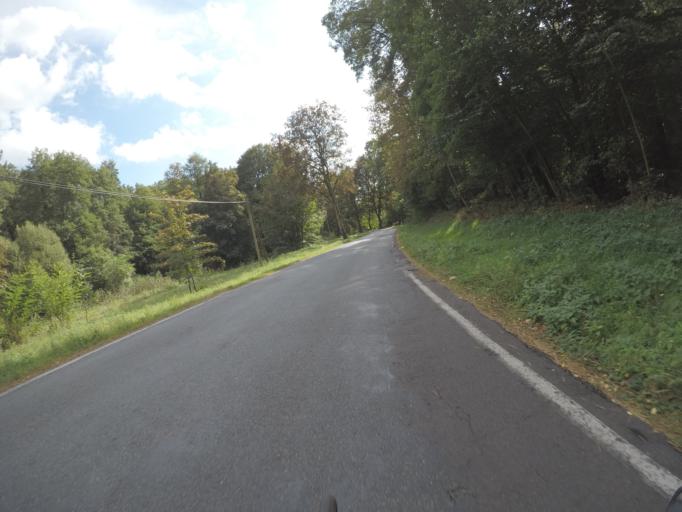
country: DE
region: Brandenburg
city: Strausberg
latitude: 52.6046
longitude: 13.8329
